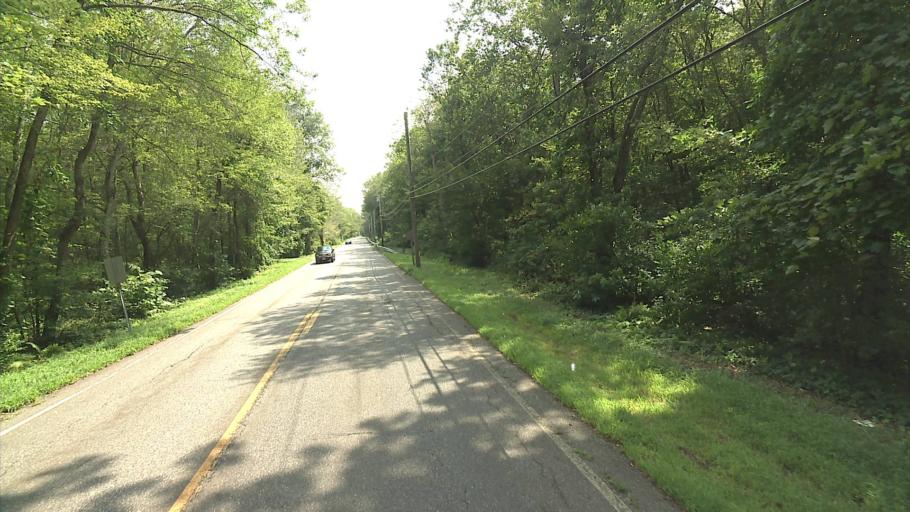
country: US
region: Connecticut
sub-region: New London County
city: Montville Center
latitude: 41.5026
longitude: -72.1901
